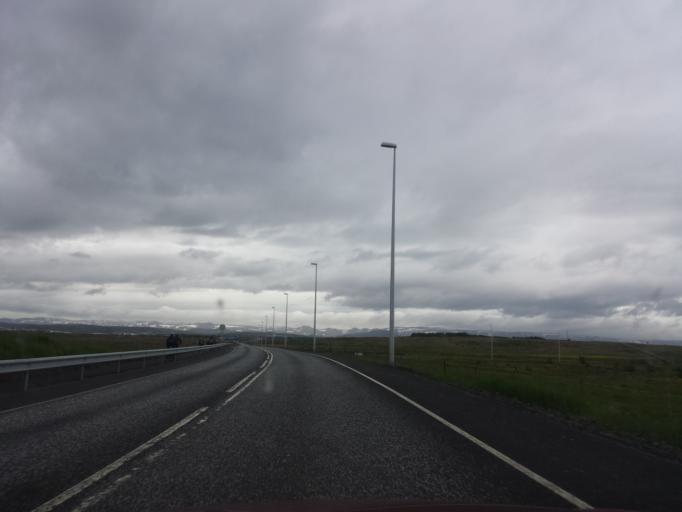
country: IS
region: Capital Region
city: Alftanes
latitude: 64.0974
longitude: -22.0042
